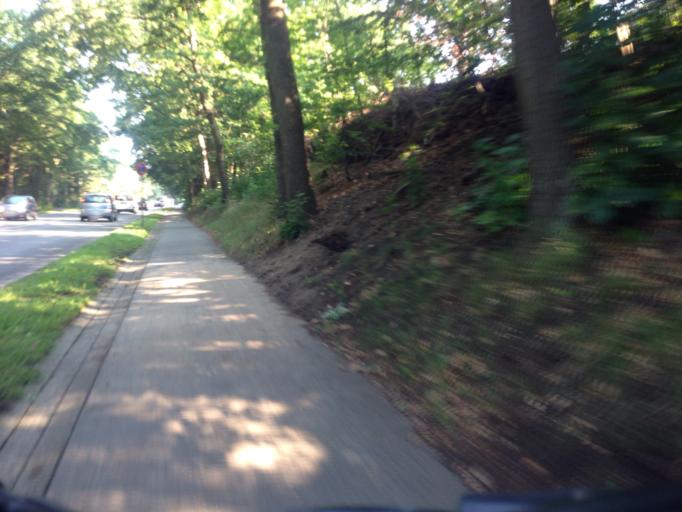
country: DE
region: Lower Saxony
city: Adendorf
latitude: 53.2770
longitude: 10.4277
